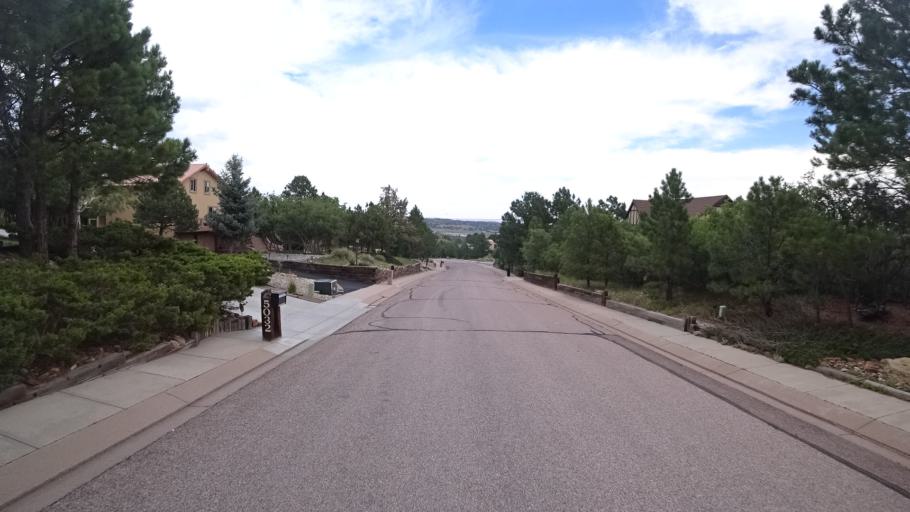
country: US
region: Colorado
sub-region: El Paso County
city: Colorado Springs
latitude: 38.9054
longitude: -104.8490
